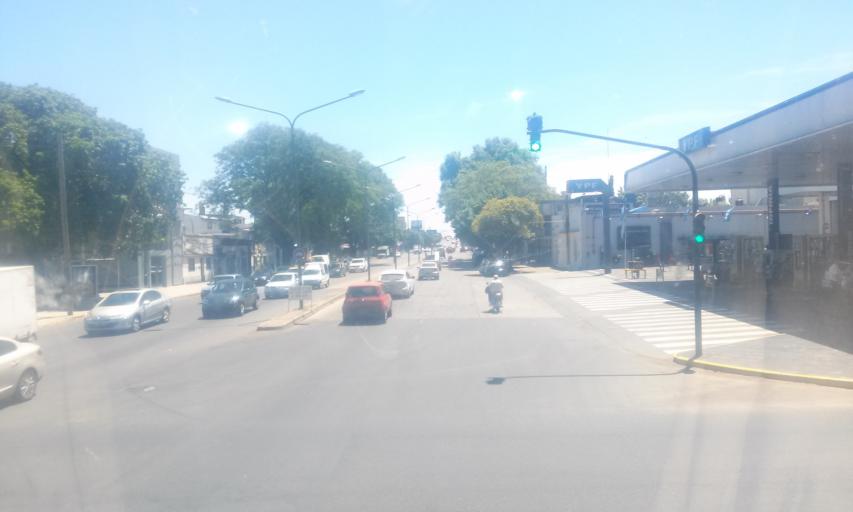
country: AR
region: Santa Fe
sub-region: Departamento de Rosario
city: Rosario
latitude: -32.9392
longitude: -60.6791
